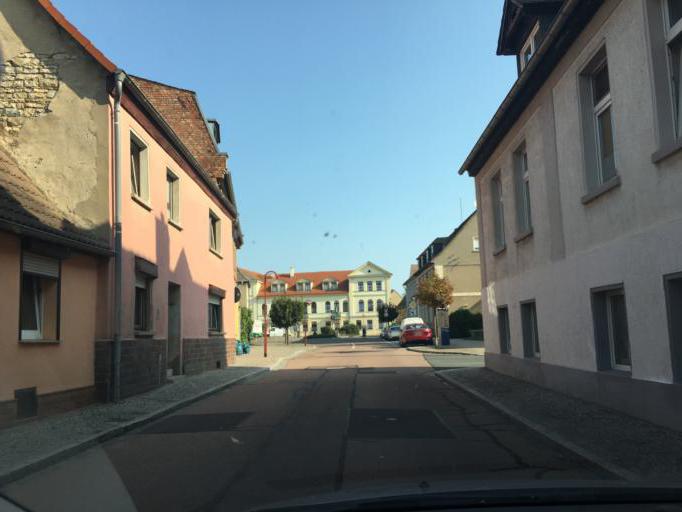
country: DE
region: Saxony-Anhalt
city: Nienburg/Saale
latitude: 51.8354
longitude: 11.7683
